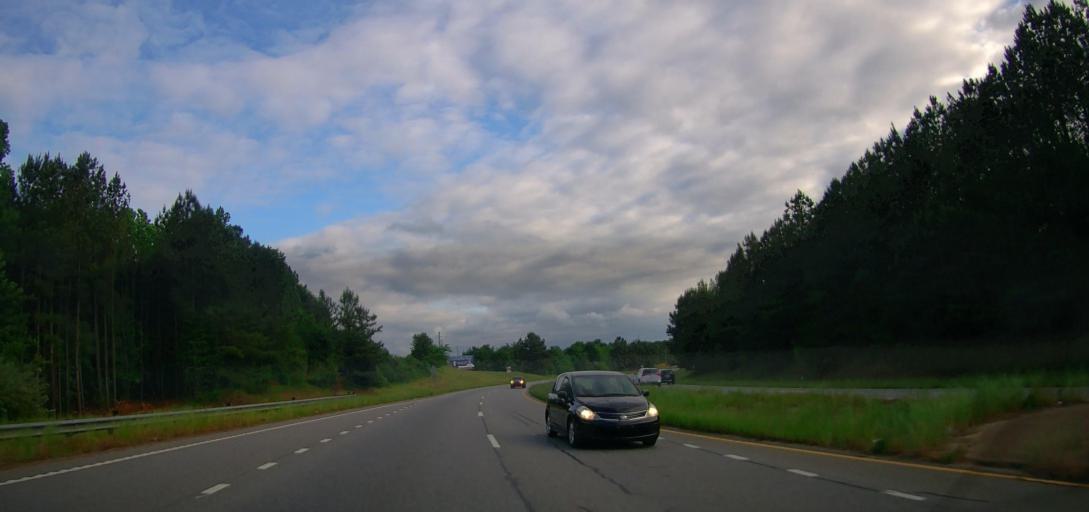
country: US
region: Georgia
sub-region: Oconee County
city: Watkinsville
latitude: 33.8851
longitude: -83.4132
